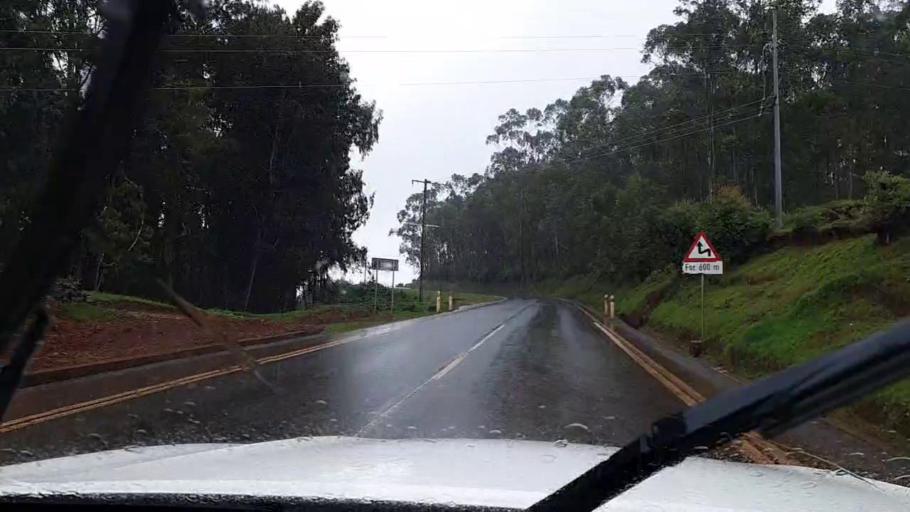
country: RW
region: Western Province
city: Cyangugu
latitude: -2.4625
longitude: 28.9949
